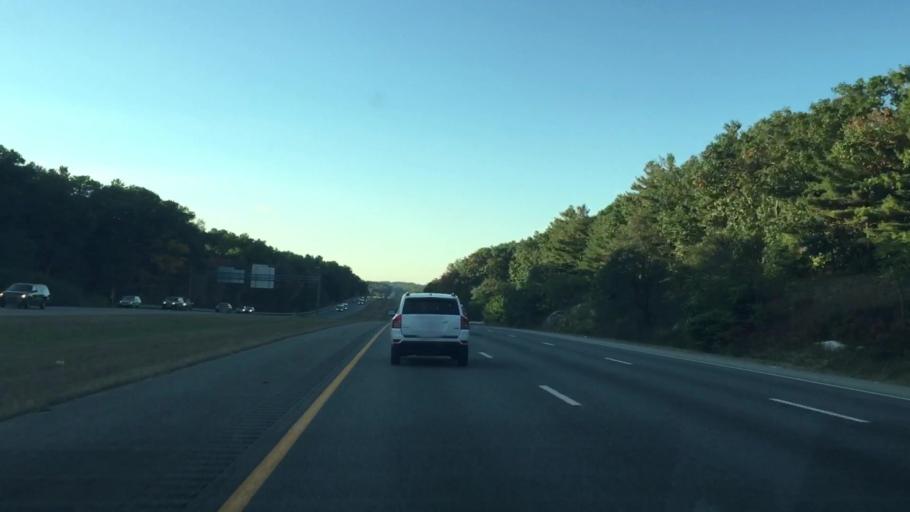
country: US
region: Massachusetts
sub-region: Middlesex County
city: Pinehurst
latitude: 42.4928
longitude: -71.2338
